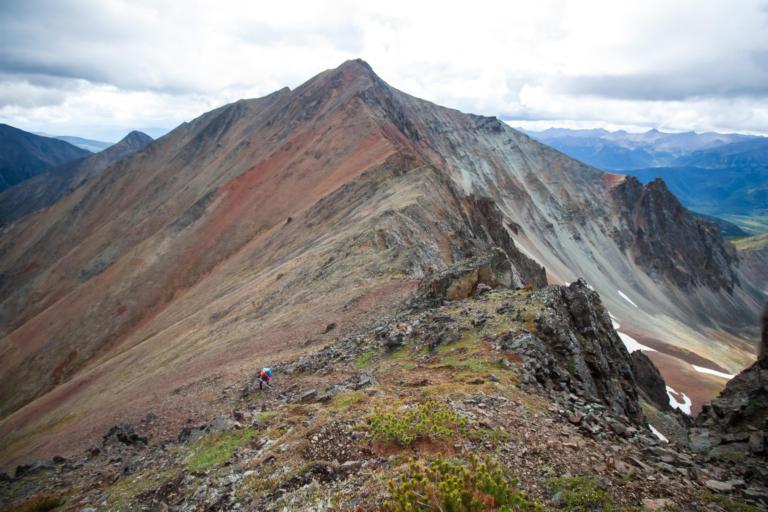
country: RU
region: Kamtsjatka
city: Yelizovo
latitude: 53.8439
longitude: 158.1885
